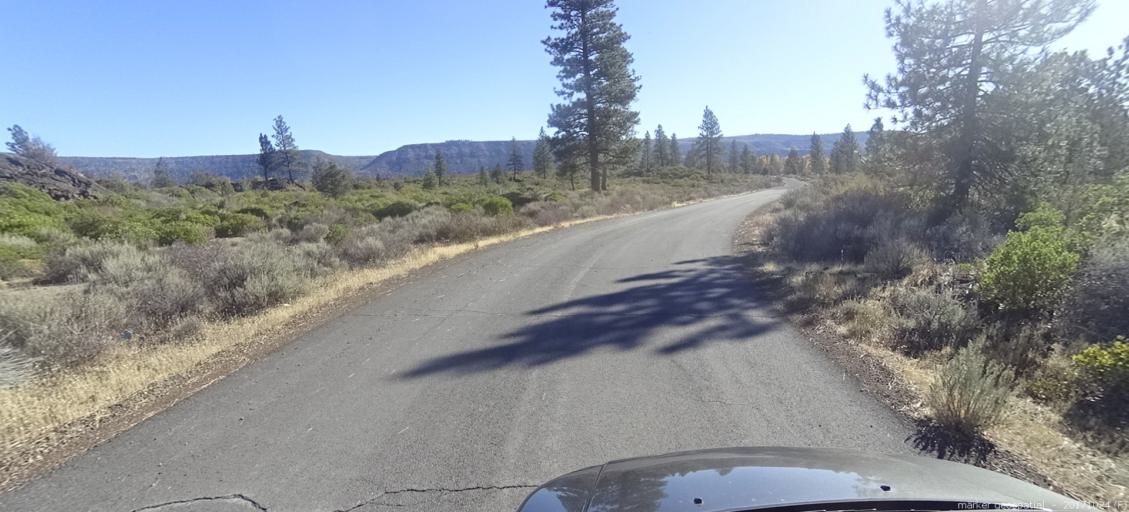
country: US
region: California
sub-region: Shasta County
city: Burney
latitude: 40.7511
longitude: -121.4593
